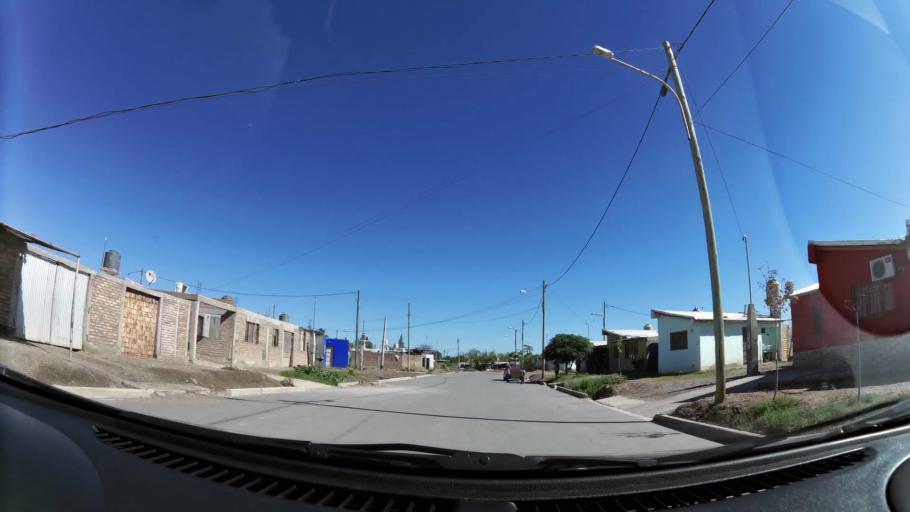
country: AR
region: Mendoza
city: Las Heras
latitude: -32.8341
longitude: -68.8179
